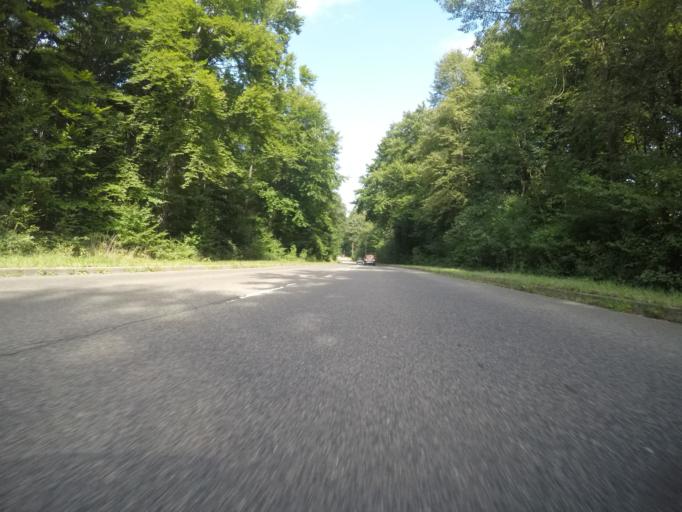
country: DE
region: Baden-Wuerttemberg
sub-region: Regierungsbezirk Stuttgart
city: Stuttgart Feuerbach
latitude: 48.7679
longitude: 9.1163
